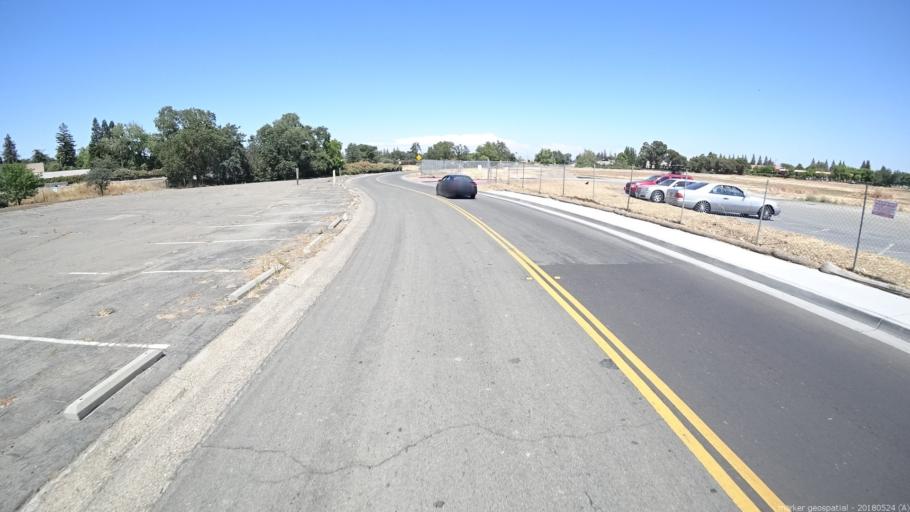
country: US
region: California
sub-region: Sacramento County
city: Sacramento
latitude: 38.5994
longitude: -121.4551
